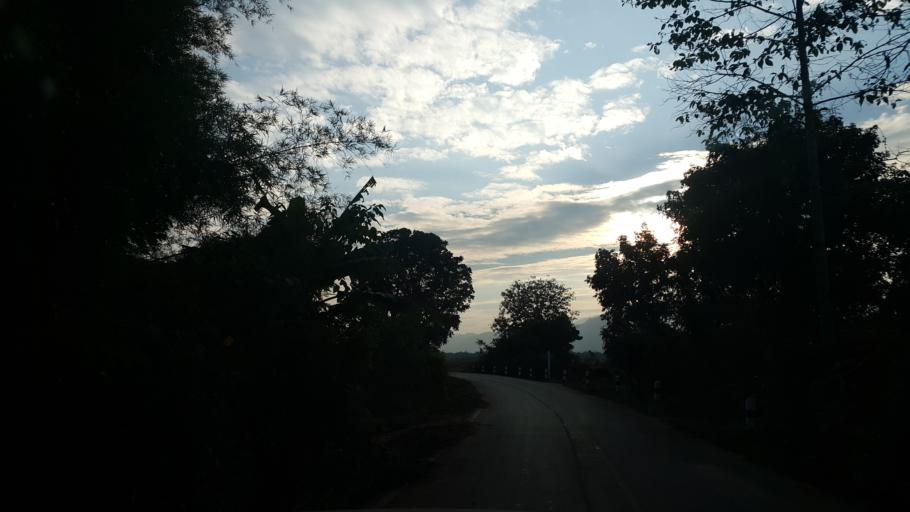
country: TH
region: Lampang
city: Sop Prap
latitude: 17.9108
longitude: 99.3302
